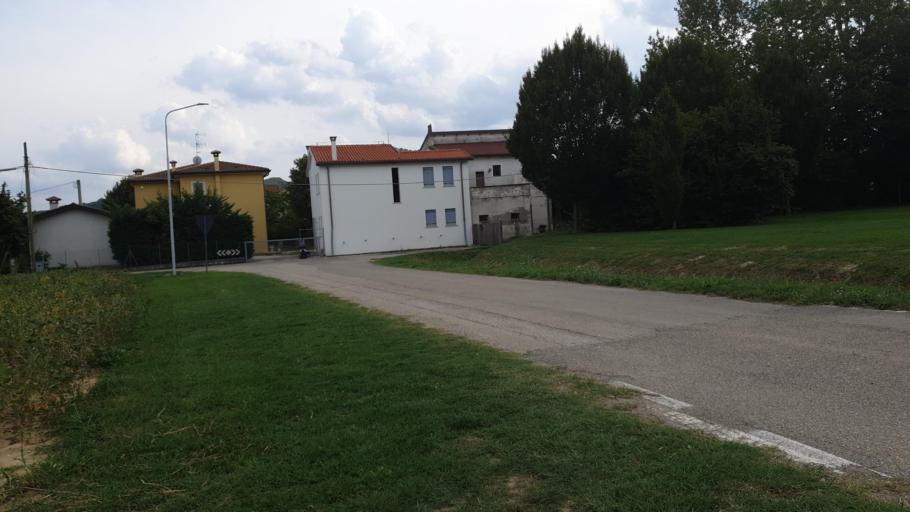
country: IT
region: Veneto
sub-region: Provincia di Padova
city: Montegrotto Terme
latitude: 45.3405
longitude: 11.7722
